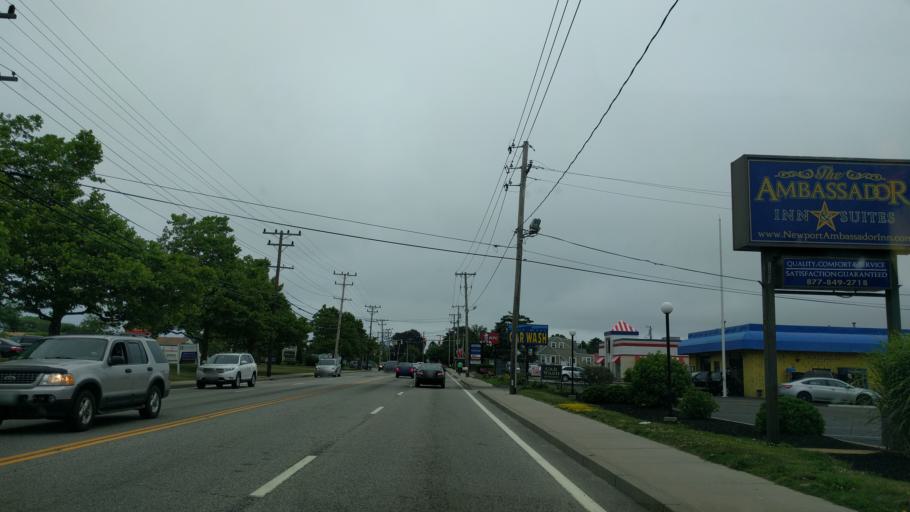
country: US
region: Rhode Island
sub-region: Newport County
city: Middletown
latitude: 41.5363
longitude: -71.2921
